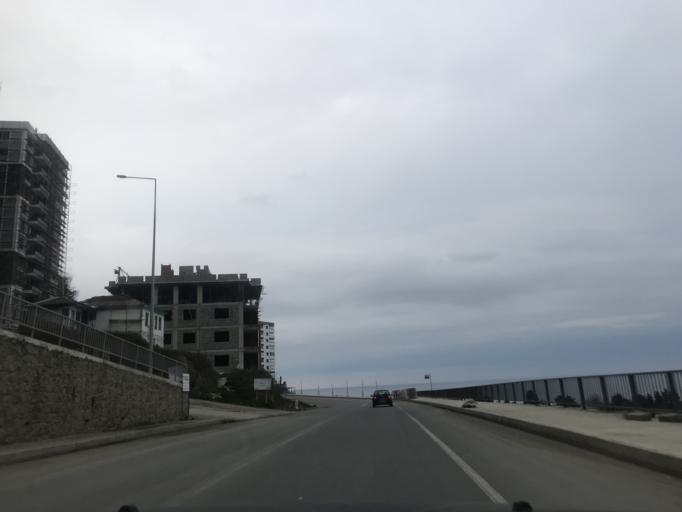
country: TR
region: Trabzon
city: Akcaabat
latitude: 41.0032
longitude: 39.6268
